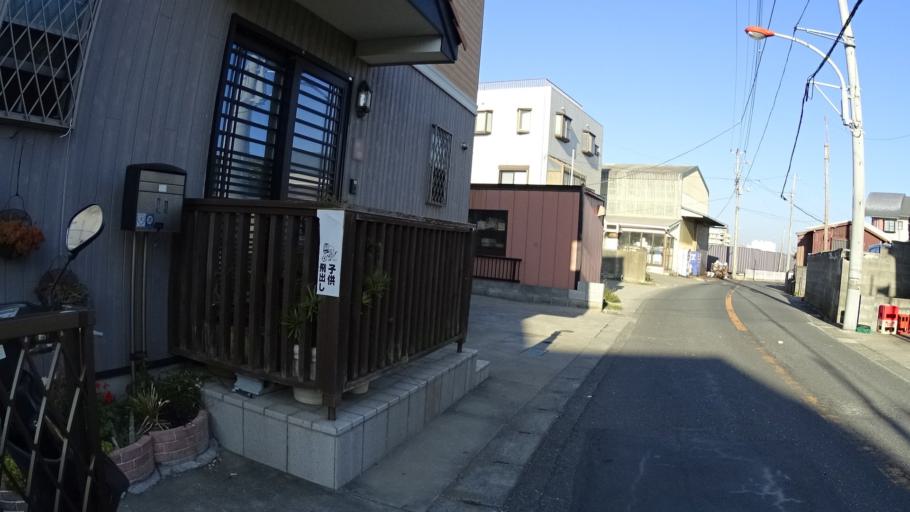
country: JP
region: Kanagawa
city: Miura
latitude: 35.2029
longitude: 139.6049
